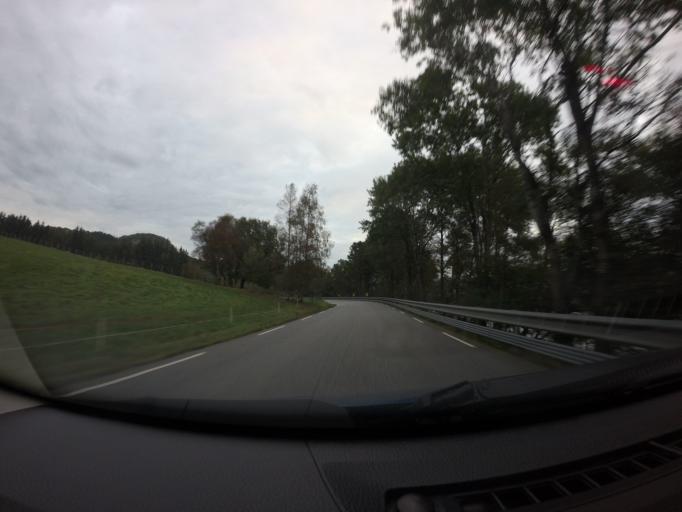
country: NO
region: Rogaland
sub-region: Gjesdal
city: Algard
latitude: 58.7735
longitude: 5.9036
